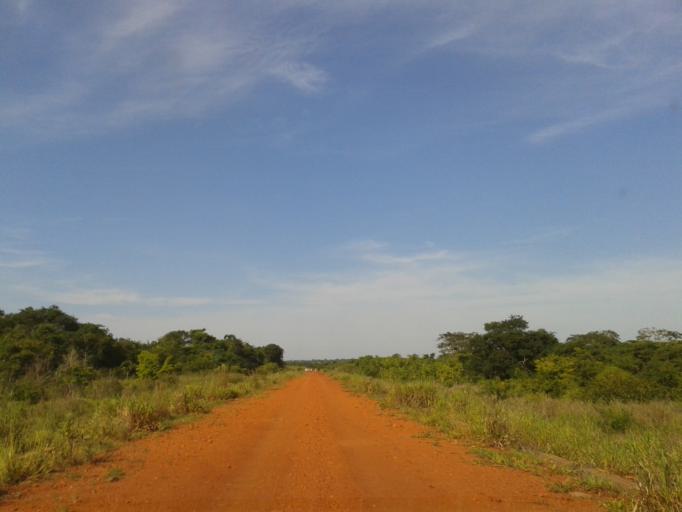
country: BR
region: Minas Gerais
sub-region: Santa Vitoria
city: Santa Vitoria
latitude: -19.1151
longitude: -50.5467
